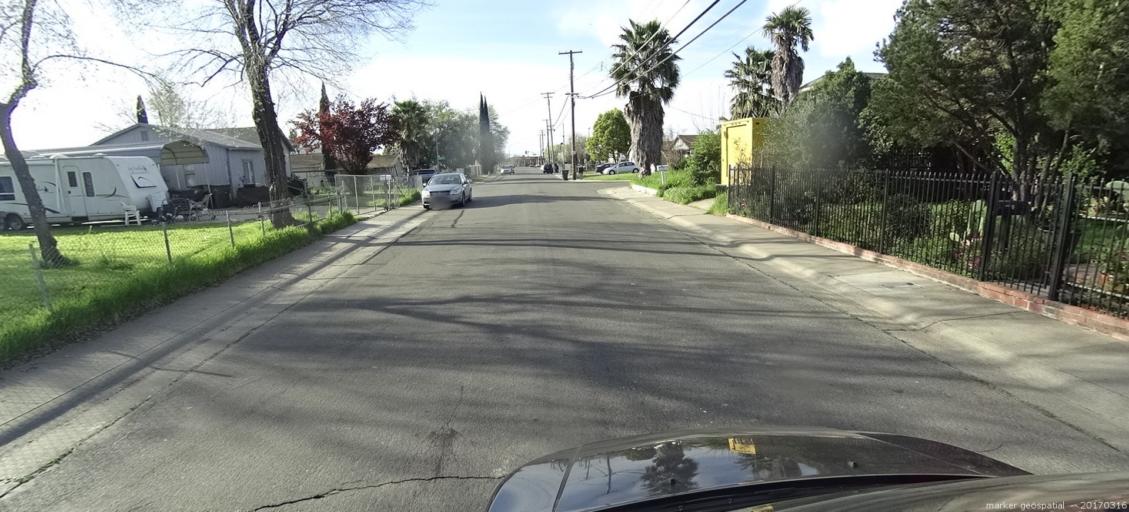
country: US
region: California
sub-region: Sacramento County
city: Parkway
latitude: 38.4981
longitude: -121.4792
